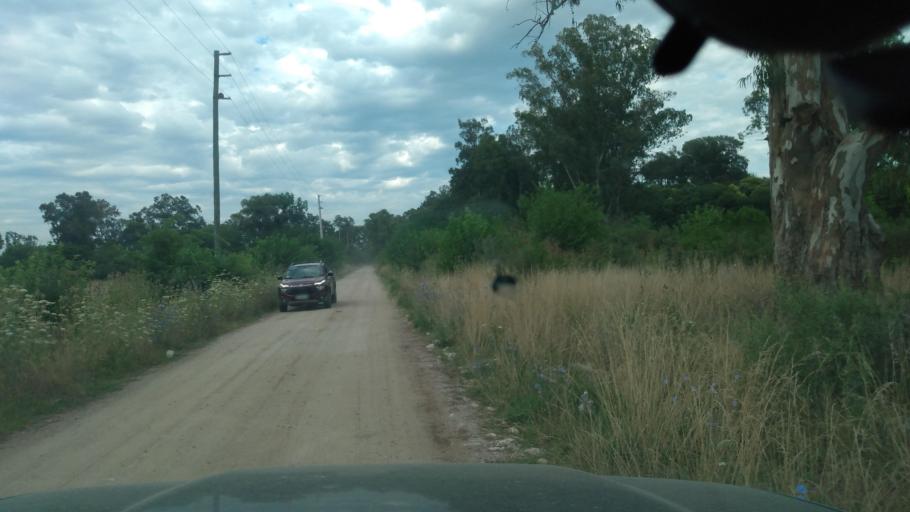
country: AR
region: Buenos Aires
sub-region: Partido de Lujan
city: Lujan
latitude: -34.5968
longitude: -59.0558
